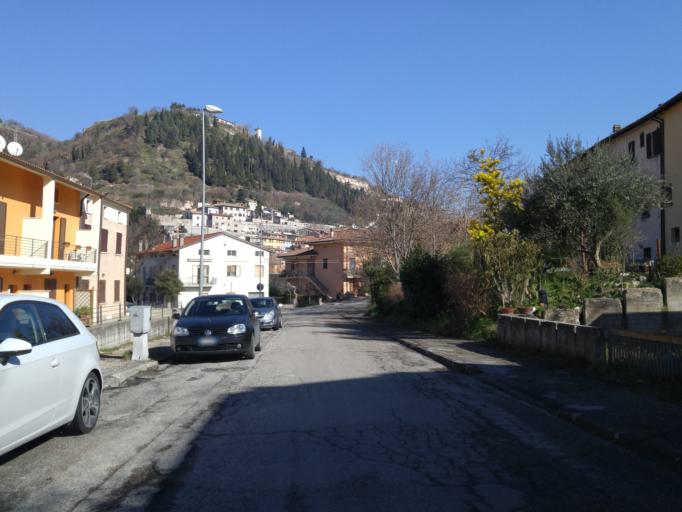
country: IT
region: The Marches
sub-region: Provincia di Pesaro e Urbino
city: Fossombrone
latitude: 43.6865
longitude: 12.8019
